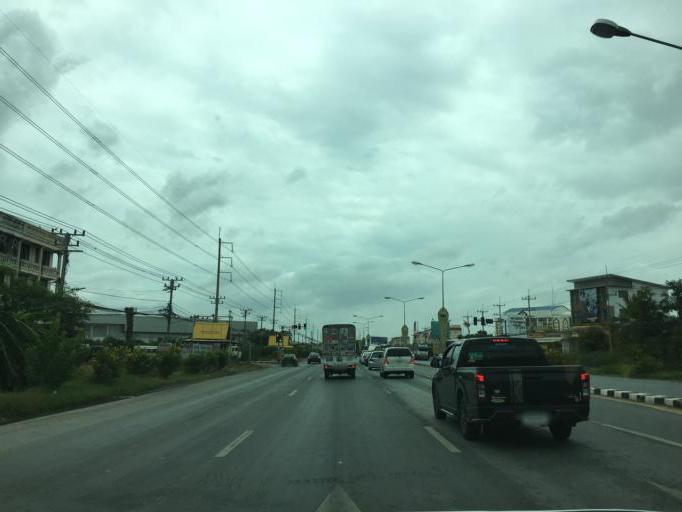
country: TH
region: Phra Nakhon Si Ayutthaya
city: Uthai
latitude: 14.2910
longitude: 100.6631
